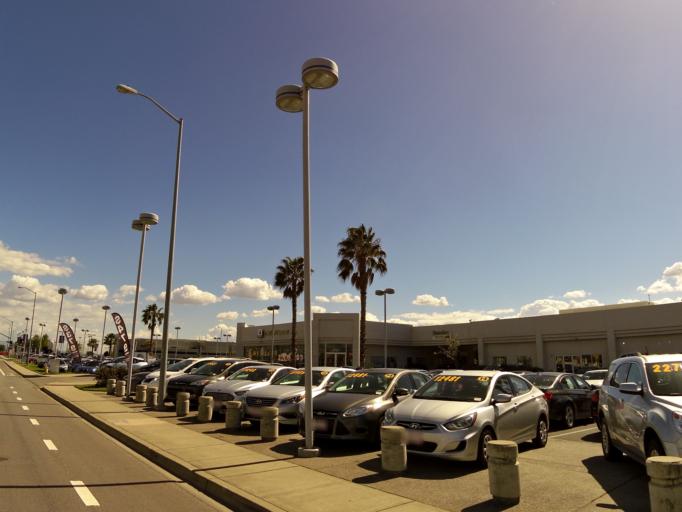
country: US
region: California
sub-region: Alameda County
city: Fremont
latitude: 37.4994
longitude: -121.9753
